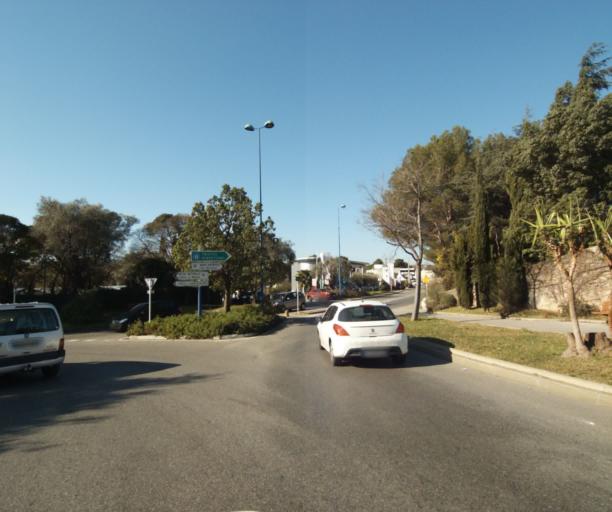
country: FR
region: Provence-Alpes-Cote d'Azur
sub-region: Departement des Alpes-Maritimes
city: Biot
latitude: 43.6024
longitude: 7.0914
